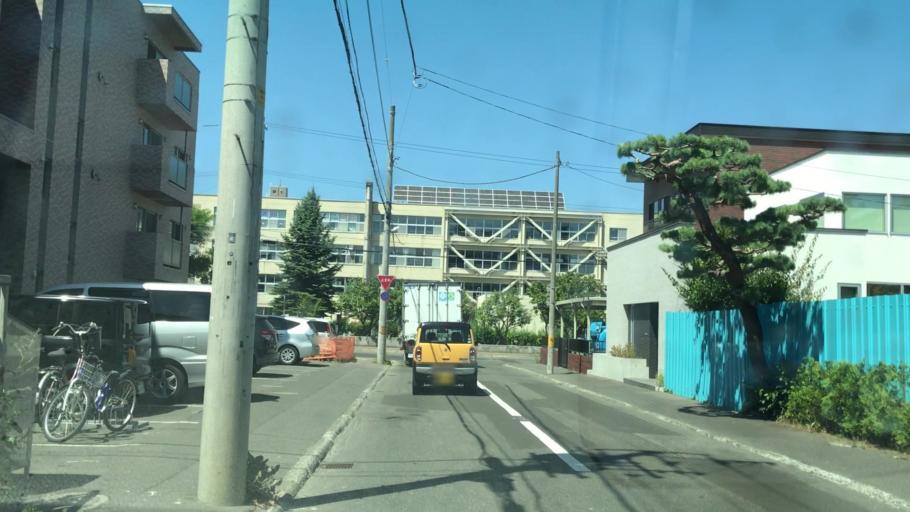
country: JP
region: Hokkaido
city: Sapporo
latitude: 43.0479
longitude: 141.3733
